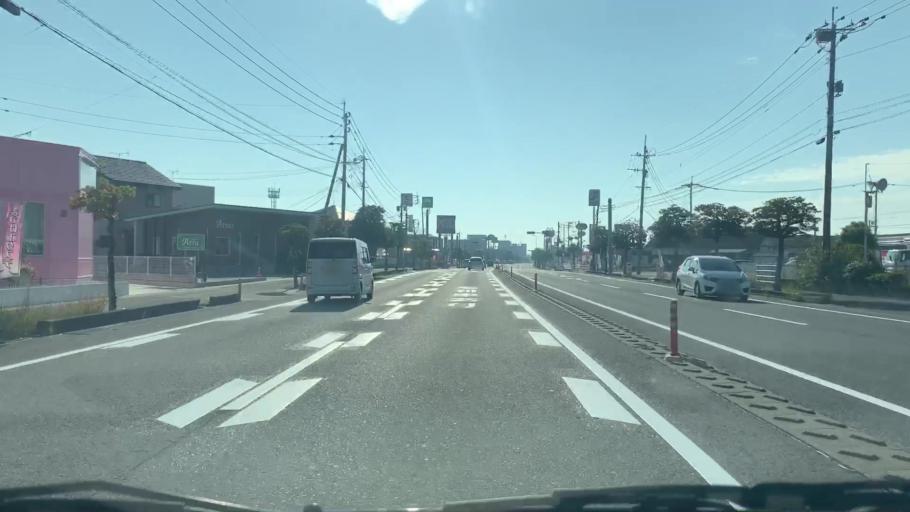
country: JP
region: Saga Prefecture
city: Saga-shi
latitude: 33.2955
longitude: 130.2831
